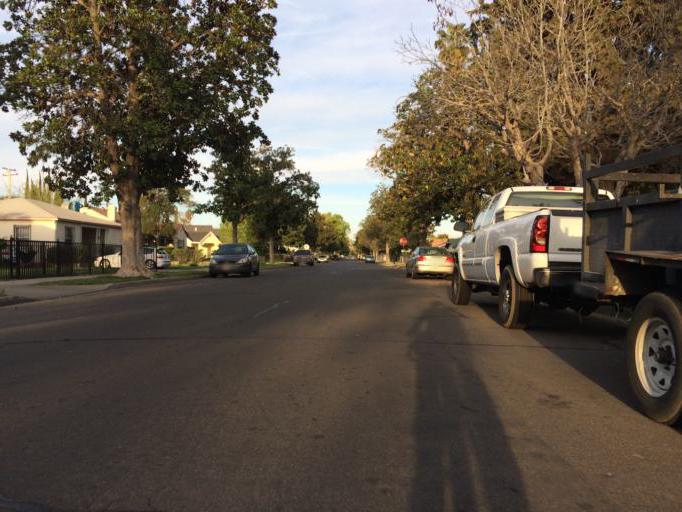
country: US
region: California
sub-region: Fresno County
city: Fresno
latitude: 36.7450
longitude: -119.7559
